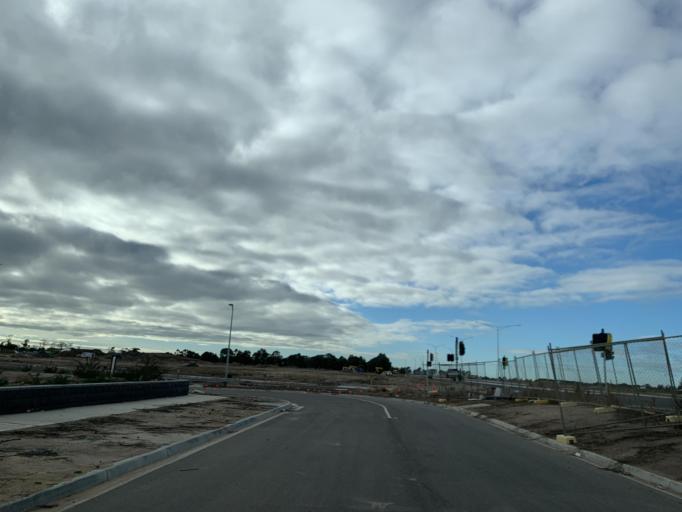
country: AU
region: Victoria
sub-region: Cardinia
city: Officer South
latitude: -38.1241
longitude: 145.3733
